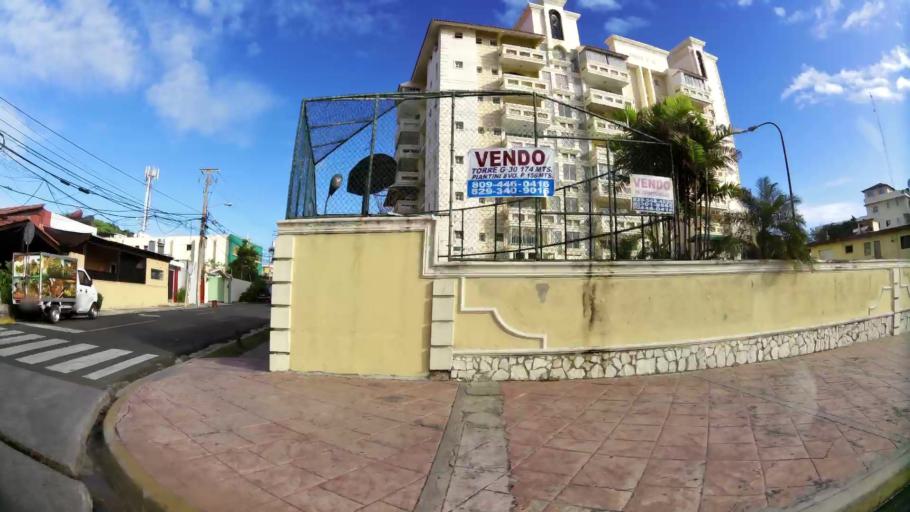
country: DO
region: Nacional
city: La Julia
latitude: 18.4563
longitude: -69.9168
